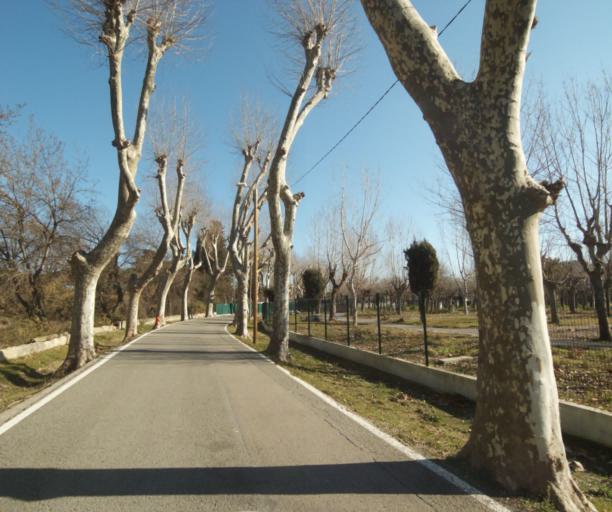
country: FR
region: Provence-Alpes-Cote d'Azur
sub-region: Departement des Alpes-Maritimes
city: Biot
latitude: 43.6127
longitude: 7.1194
